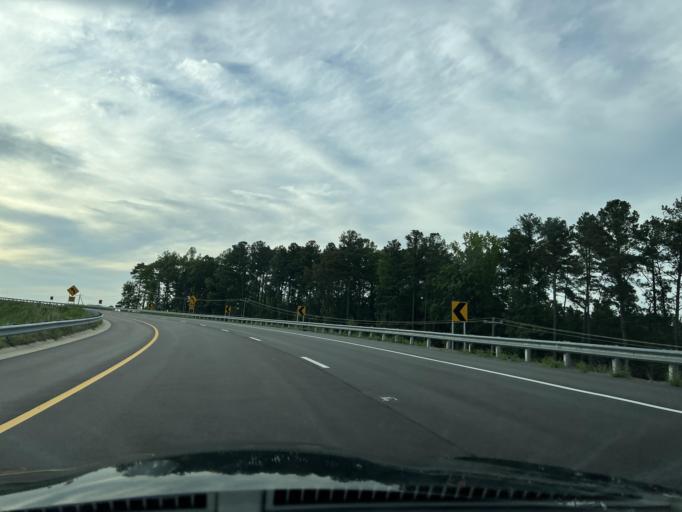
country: US
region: North Carolina
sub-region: Durham County
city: Durham
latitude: 35.9751
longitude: -78.8518
